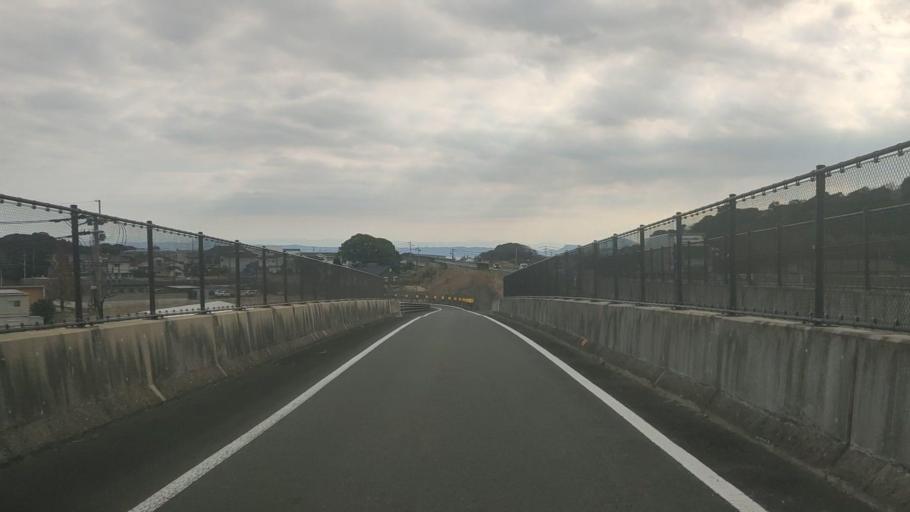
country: JP
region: Nagasaki
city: Shimabara
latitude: 32.7628
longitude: 130.3626
